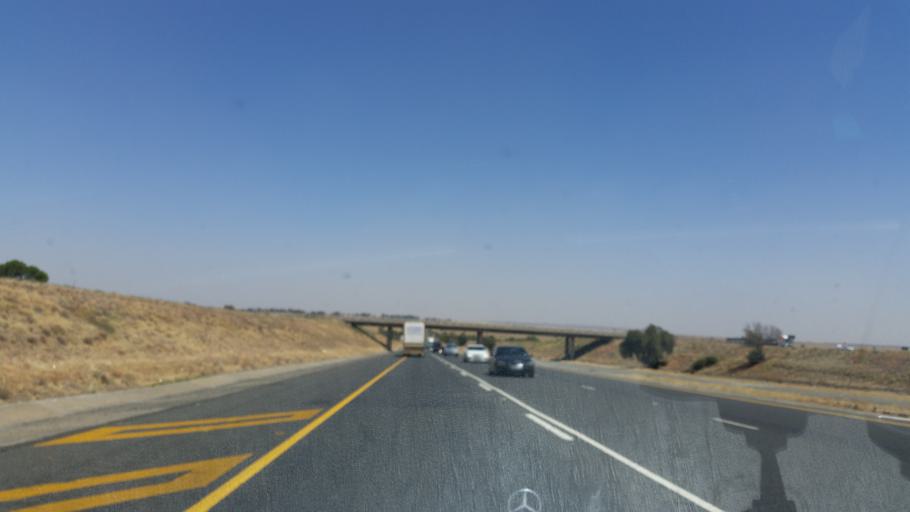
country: ZA
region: Orange Free State
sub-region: Lejweleputswa District Municipality
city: Winburg
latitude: -28.6263
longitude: 26.9115
